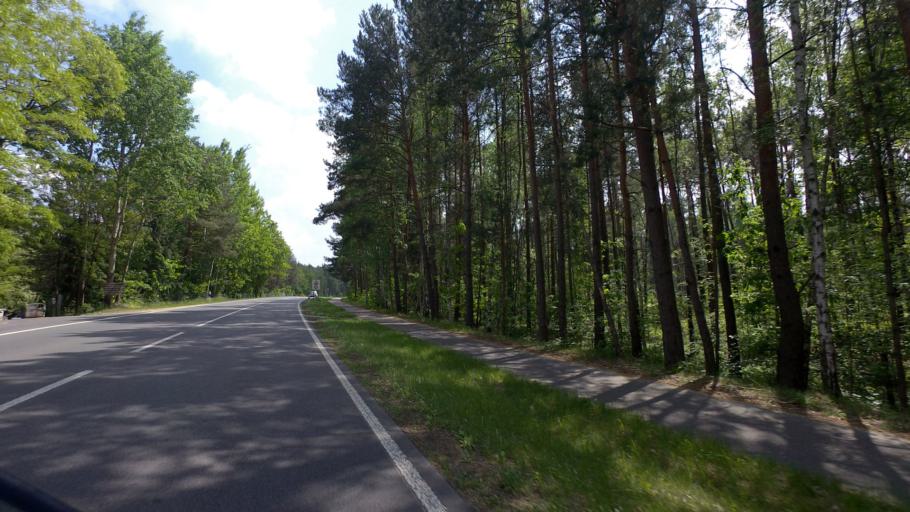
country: DE
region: Saxony
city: Trebendorf
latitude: 51.5270
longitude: 14.6030
